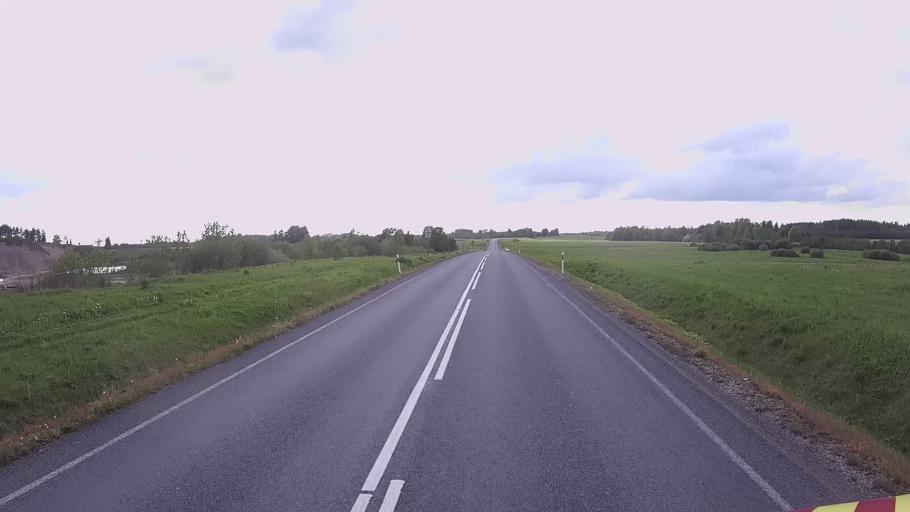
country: EE
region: Jogevamaa
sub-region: Mustvee linn
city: Mustvee
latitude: 59.0381
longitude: 27.0760
